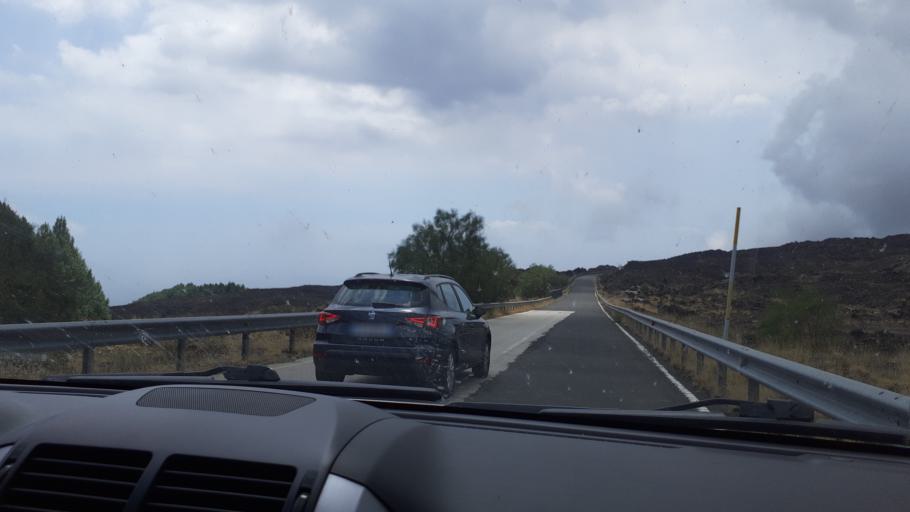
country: IT
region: Sicily
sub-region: Catania
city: Nicolosi
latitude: 37.6921
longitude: 15.0210
